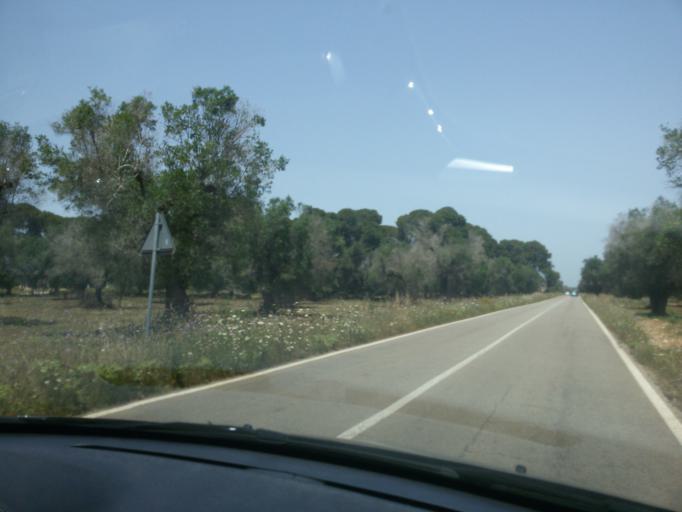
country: IT
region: Apulia
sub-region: Provincia di Lecce
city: Porto Cesareo
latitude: 40.3066
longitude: 17.9197
